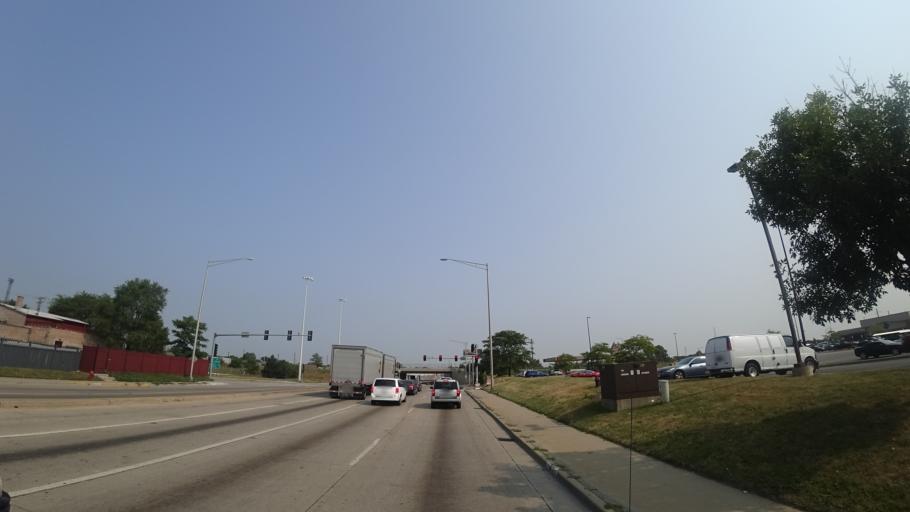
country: US
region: Illinois
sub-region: Cook County
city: Cicero
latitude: 41.8424
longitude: -87.7438
